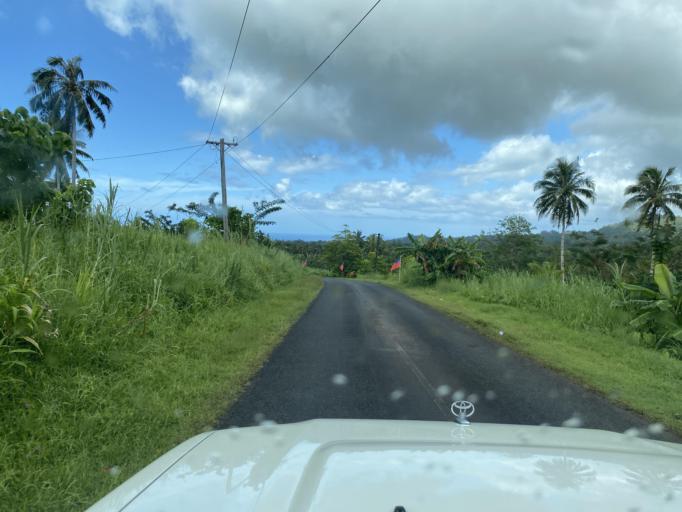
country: WS
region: Va`a-o-Fonoti
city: Samamea
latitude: -13.9744
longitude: -171.5834
